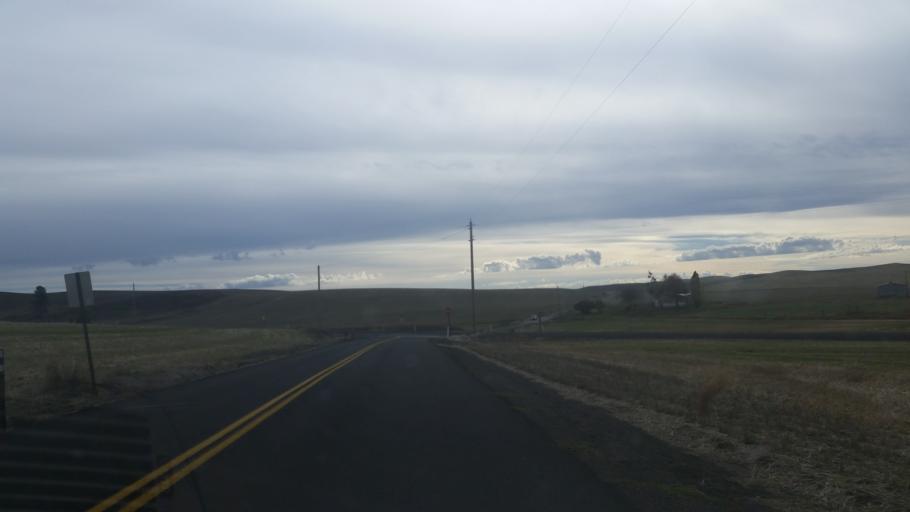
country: US
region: Washington
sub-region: Spokane County
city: Cheney
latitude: 47.3048
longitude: -117.4930
